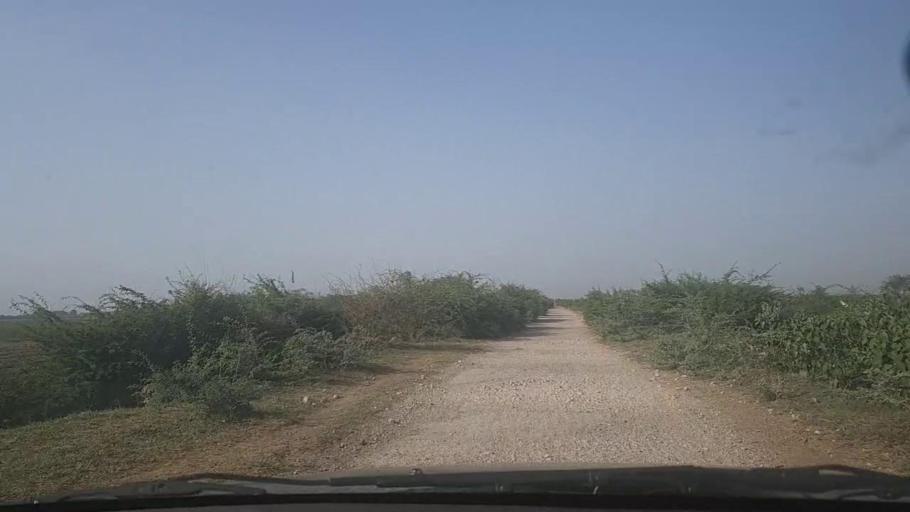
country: PK
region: Sindh
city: Keti Bandar
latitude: 24.2523
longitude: 67.5618
